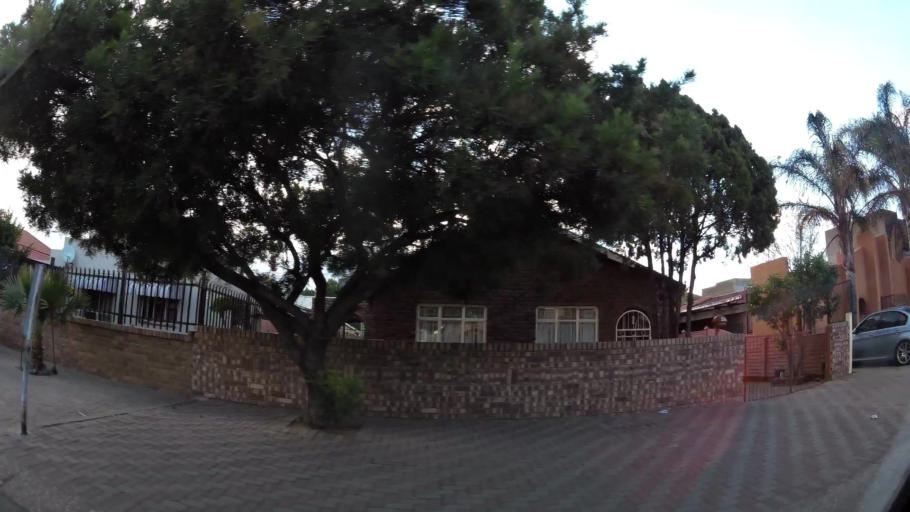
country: ZA
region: Limpopo
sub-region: Capricorn District Municipality
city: Polokwane
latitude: -23.9057
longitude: 29.4291
